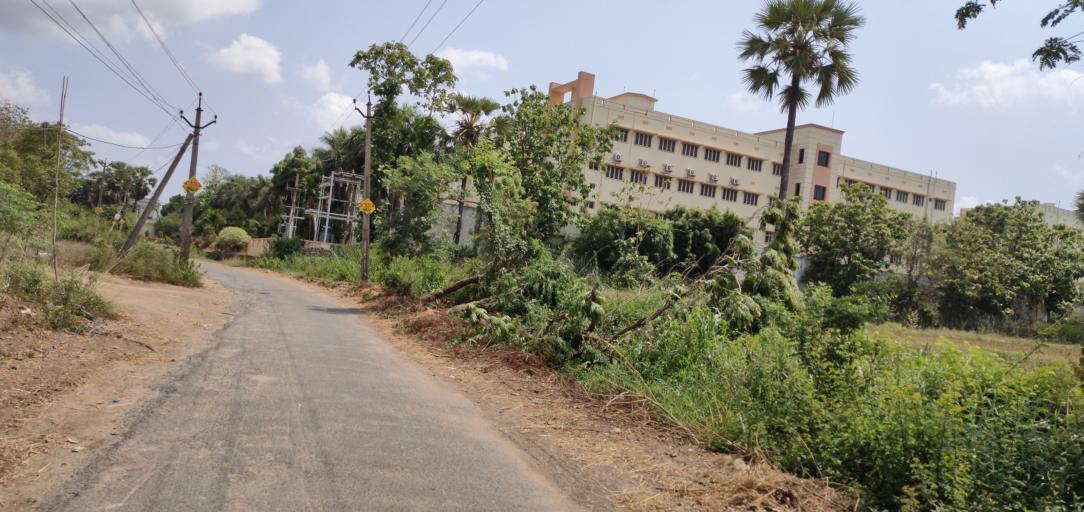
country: IN
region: Andhra Pradesh
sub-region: West Godavari
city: Tadepallegudem
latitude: 16.8569
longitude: 81.4941
